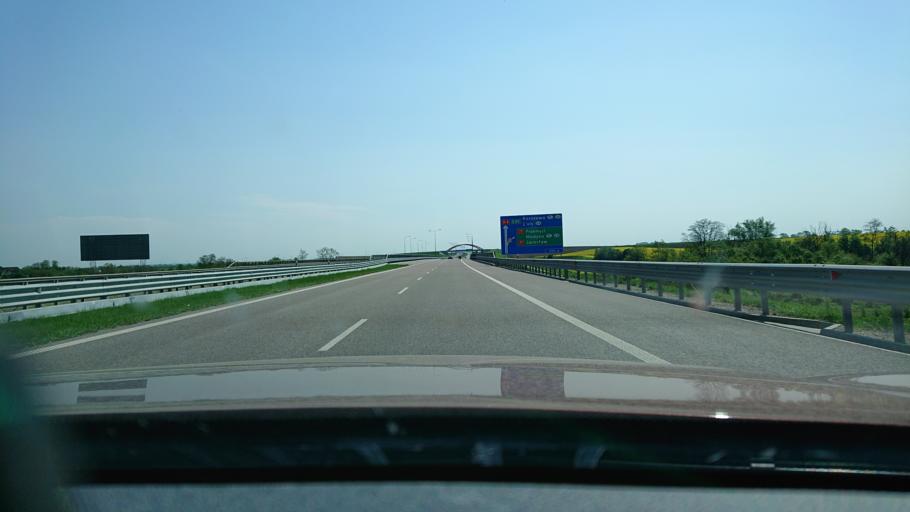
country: PL
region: Subcarpathian Voivodeship
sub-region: Powiat przemyski
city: Orly
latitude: 49.9138
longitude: 22.7948
